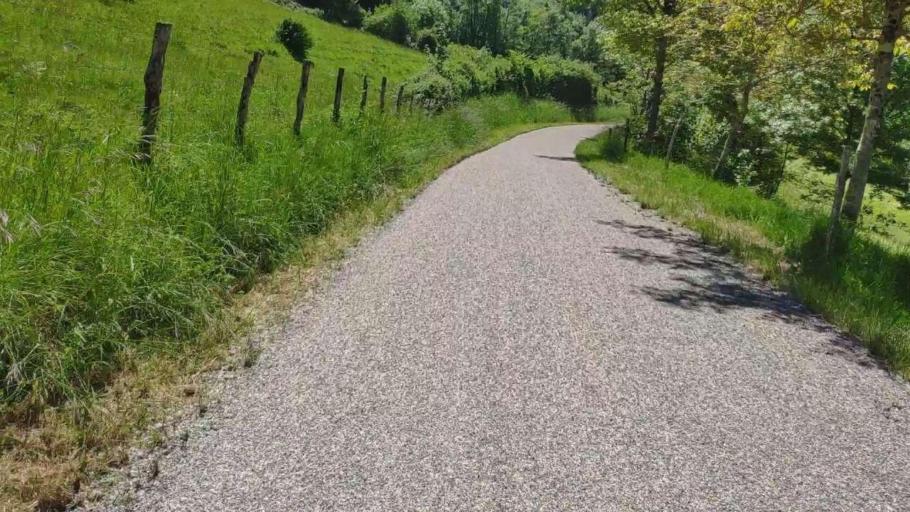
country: FR
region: Franche-Comte
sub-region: Departement du Jura
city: Poligny
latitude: 46.7522
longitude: 5.6742
